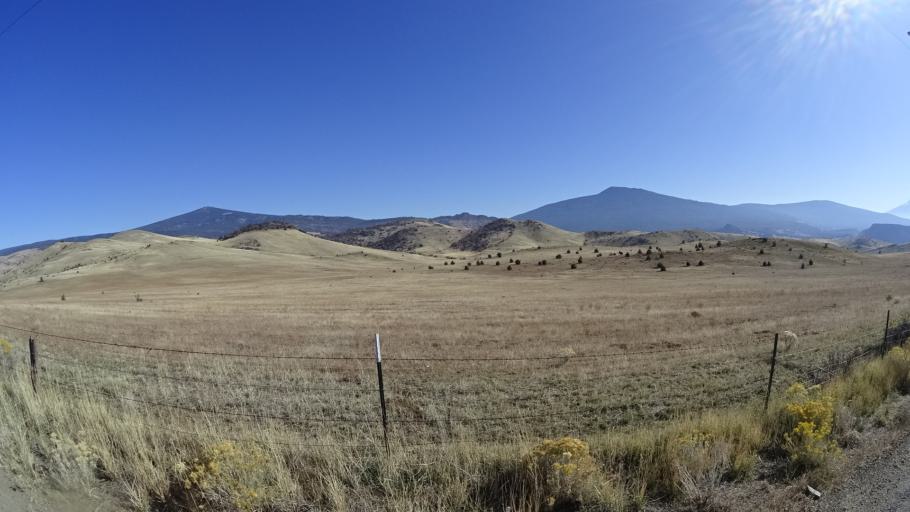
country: US
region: California
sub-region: Siskiyou County
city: Montague
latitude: 41.7732
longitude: -122.3590
